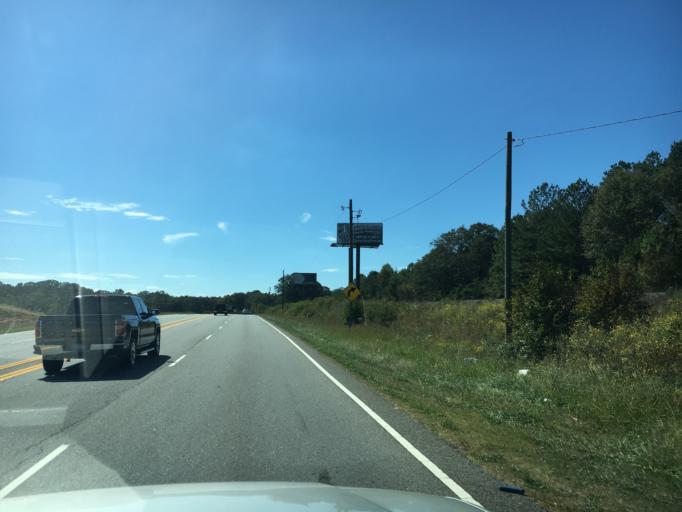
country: US
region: South Carolina
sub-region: Pickens County
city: Clemson
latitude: 34.6921
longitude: -82.8587
